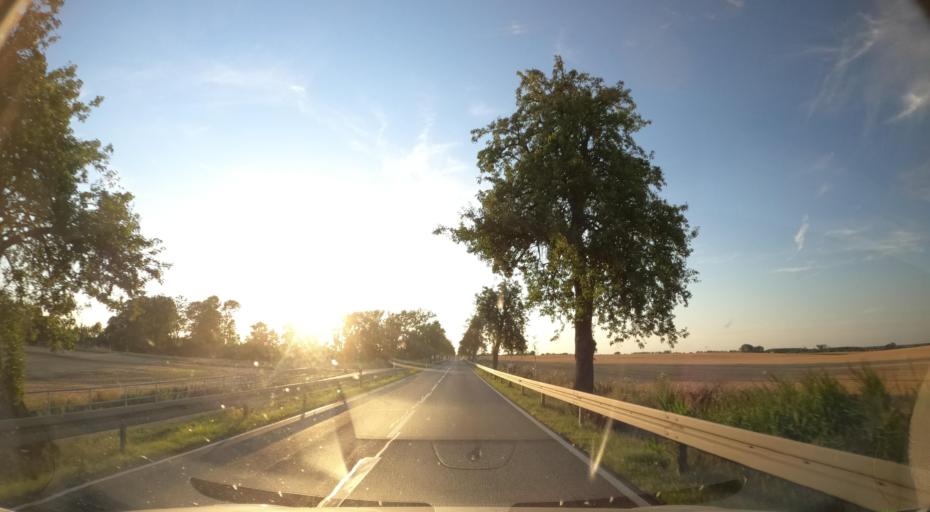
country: DE
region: Mecklenburg-Vorpommern
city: Viereck
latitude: 53.4865
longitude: 14.1024
